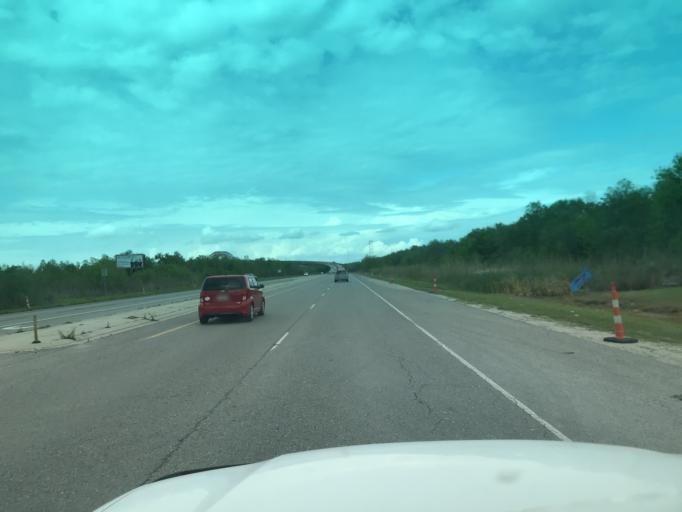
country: US
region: Louisiana
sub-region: Saint Bernard Parish
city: Chalmette
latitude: 29.9913
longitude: -89.9425
